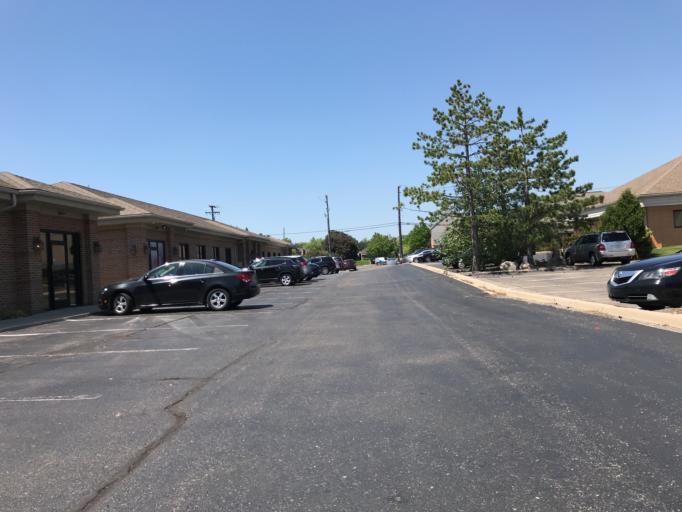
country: US
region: Michigan
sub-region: Oakland County
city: West Bloomfield Township
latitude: 42.5417
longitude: -83.3632
